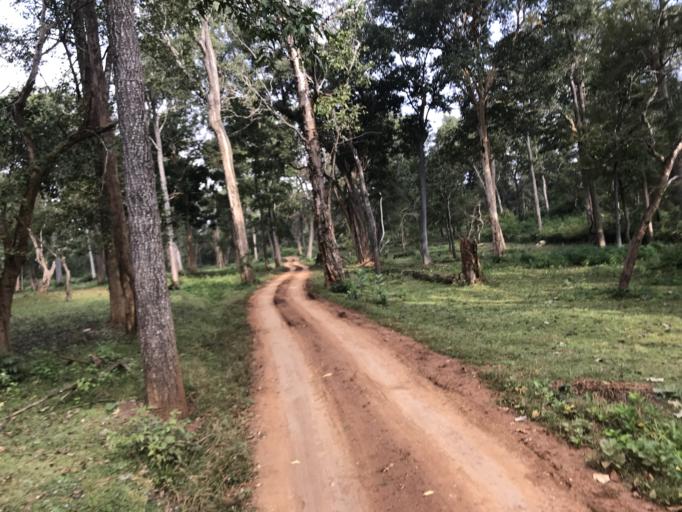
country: IN
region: Karnataka
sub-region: Mysore
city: Heggadadevankote
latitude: 11.9753
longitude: 76.1956
